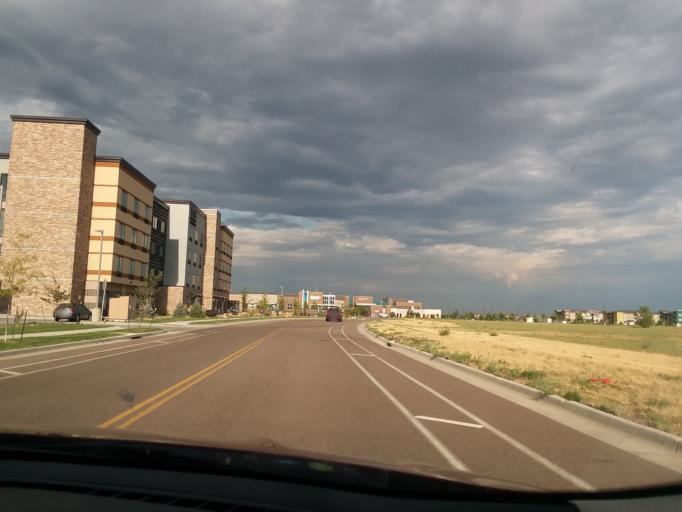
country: US
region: Colorado
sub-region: Larimer County
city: Fort Collins
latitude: 40.5215
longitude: -105.0139
